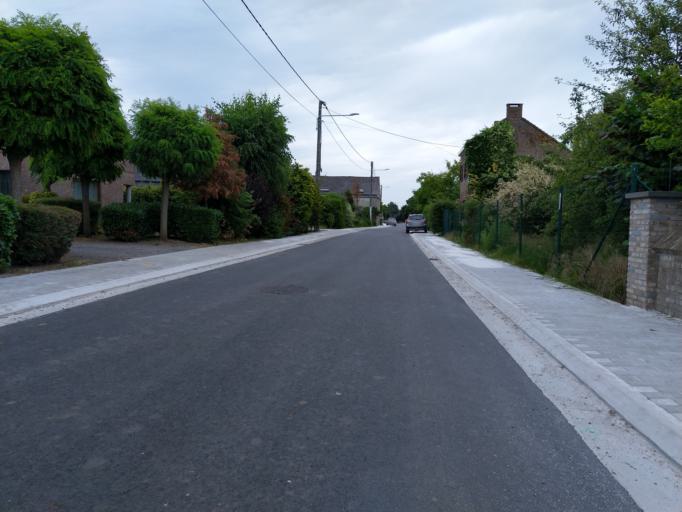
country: BE
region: Wallonia
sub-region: Province du Hainaut
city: Mons
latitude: 50.4669
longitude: 3.9789
